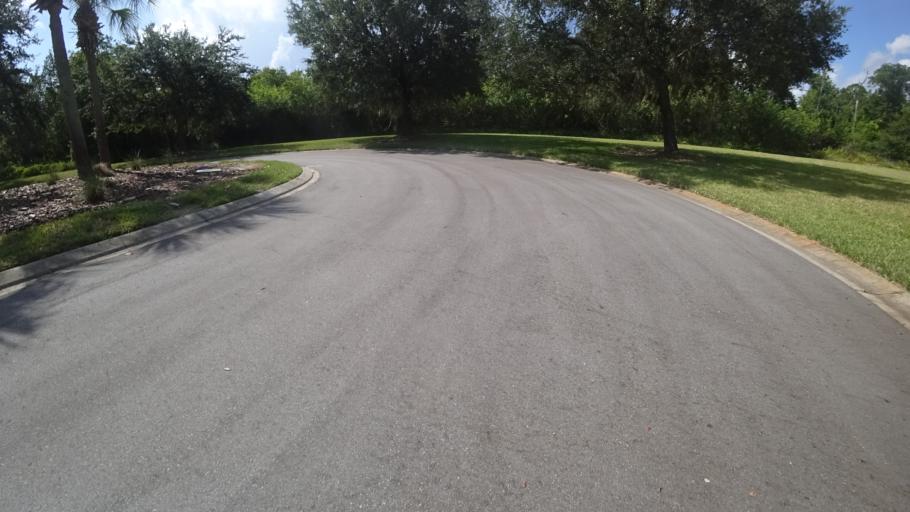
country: US
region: Florida
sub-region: Sarasota County
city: The Meadows
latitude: 27.4143
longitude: -82.4223
